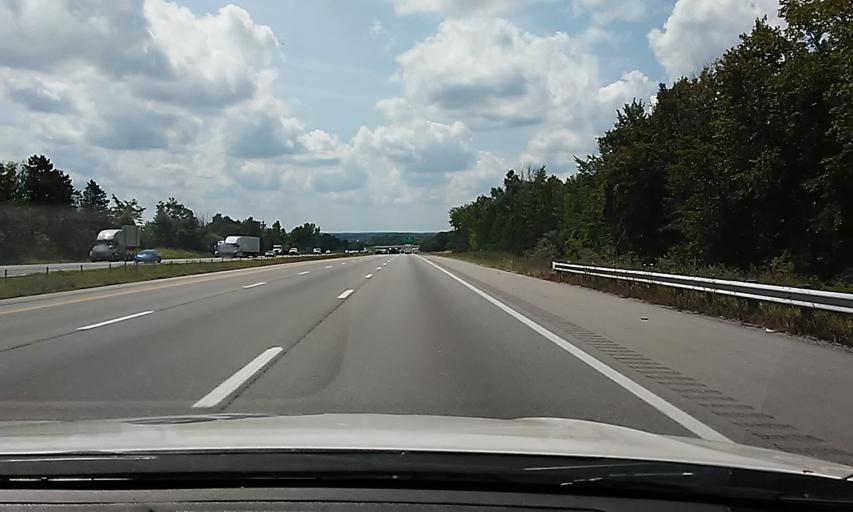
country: US
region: Ohio
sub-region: Morrow County
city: Mount Gilead
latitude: 40.5112
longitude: -82.6961
